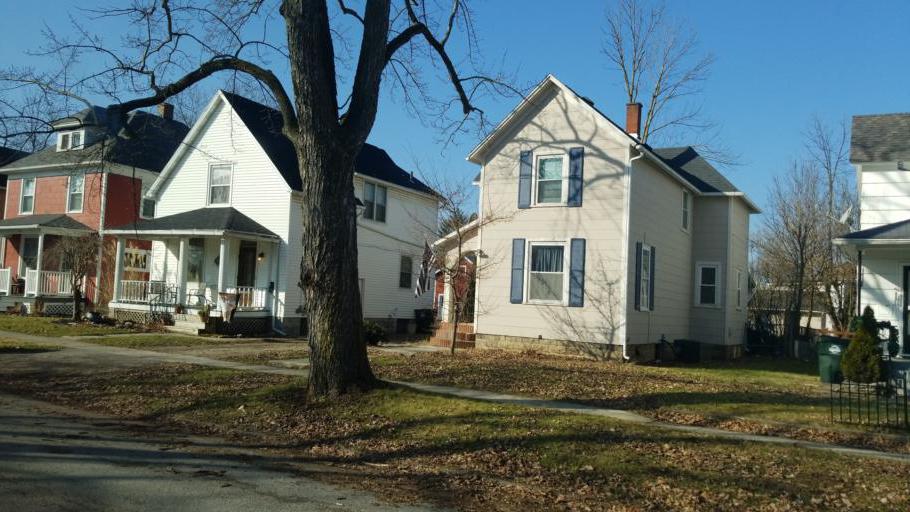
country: US
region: Ohio
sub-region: Seneca County
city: Tiffin
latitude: 41.1089
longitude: -83.1697
